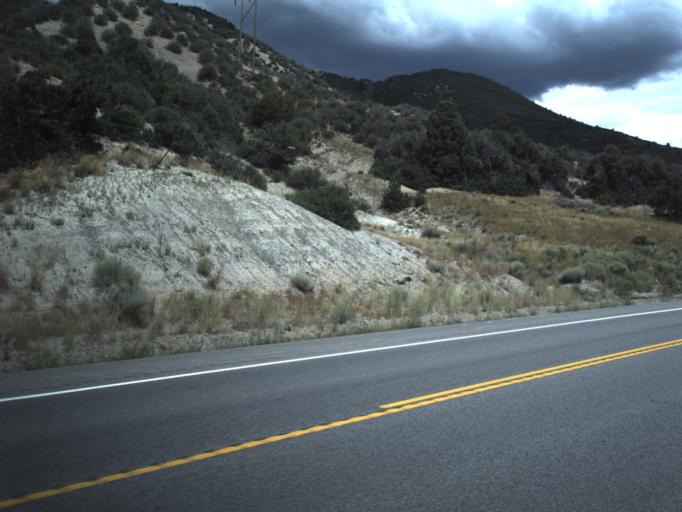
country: US
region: Utah
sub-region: Carbon County
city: Helper
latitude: 39.9366
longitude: -111.1369
